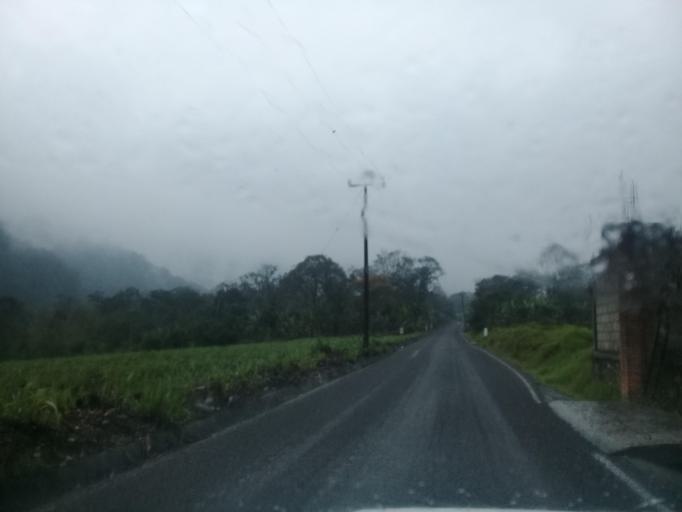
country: MX
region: Veracruz
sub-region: Amatlan de los Reyes
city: Centro de Readaptacion Social
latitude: 18.7989
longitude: -96.9370
